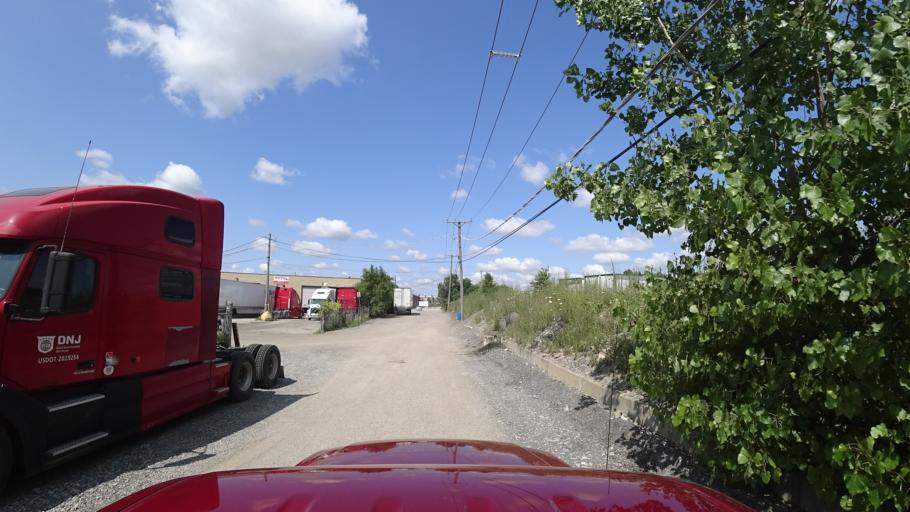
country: US
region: Illinois
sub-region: Cook County
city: Cicero
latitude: 41.8320
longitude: -87.7409
